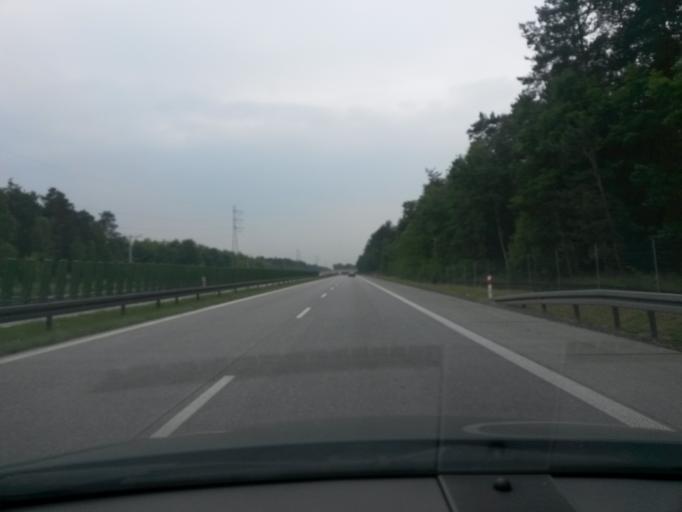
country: PL
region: Lodz Voivodeship
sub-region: Powiat piotrkowski
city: Moszczenica
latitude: 51.4555
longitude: 19.7736
